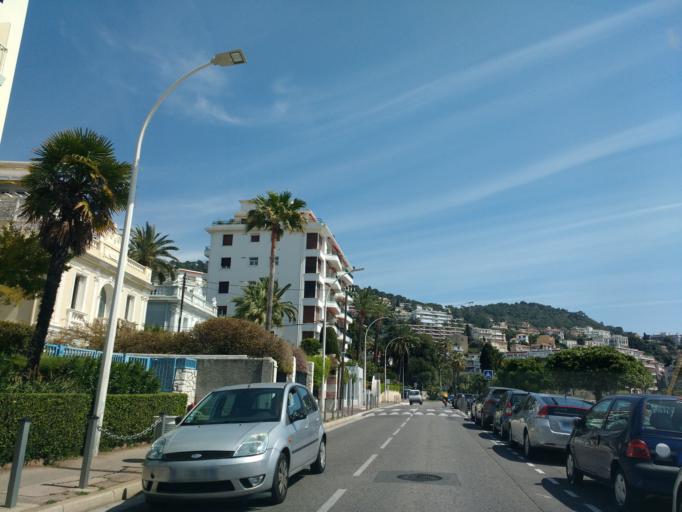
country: FR
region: Provence-Alpes-Cote d'Azur
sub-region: Departement des Alpes-Maritimes
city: Villefranche-sur-Mer
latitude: 43.6941
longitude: 7.2883
